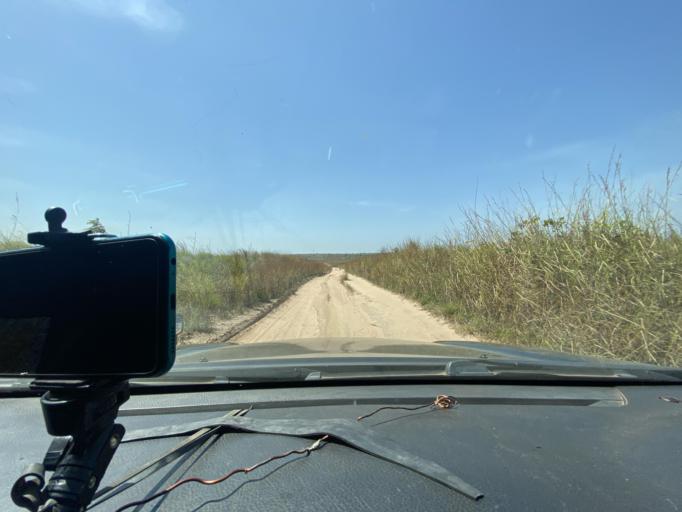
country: CD
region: Kasai-Oriental
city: Kabinda
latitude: -5.9342
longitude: 24.8210
